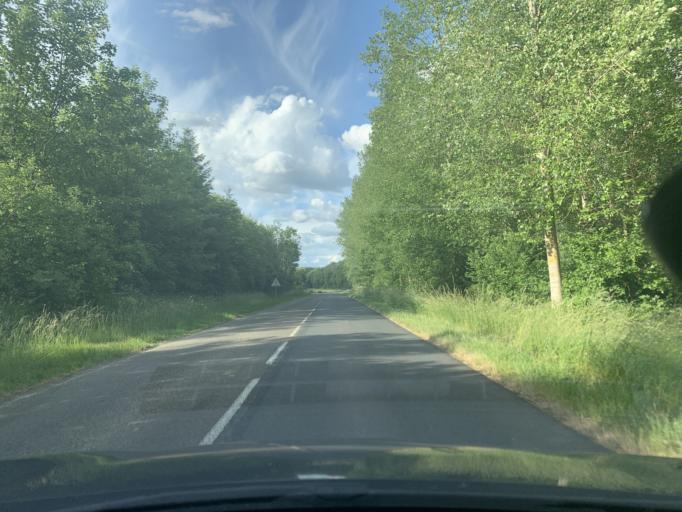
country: FR
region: Nord-Pas-de-Calais
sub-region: Departement du Nord
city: Gouzeaucourt
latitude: 50.0835
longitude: 3.1415
